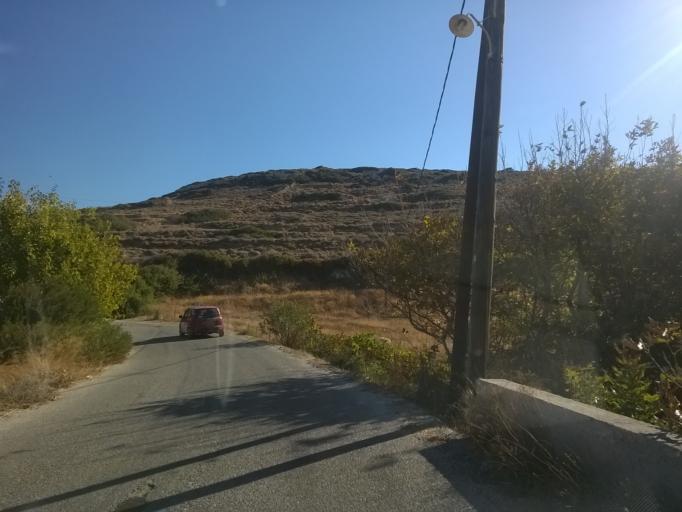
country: GR
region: South Aegean
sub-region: Nomos Kykladon
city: Naxos
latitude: 37.1382
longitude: 25.4520
